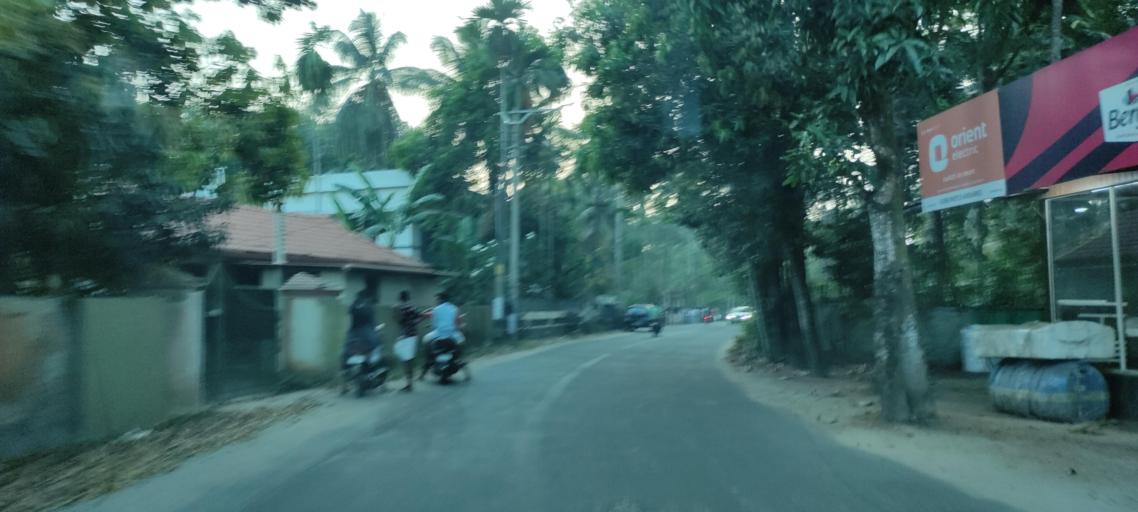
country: IN
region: Kerala
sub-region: Alappuzha
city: Kayankulam
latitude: 9.1210
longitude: 76.4940
